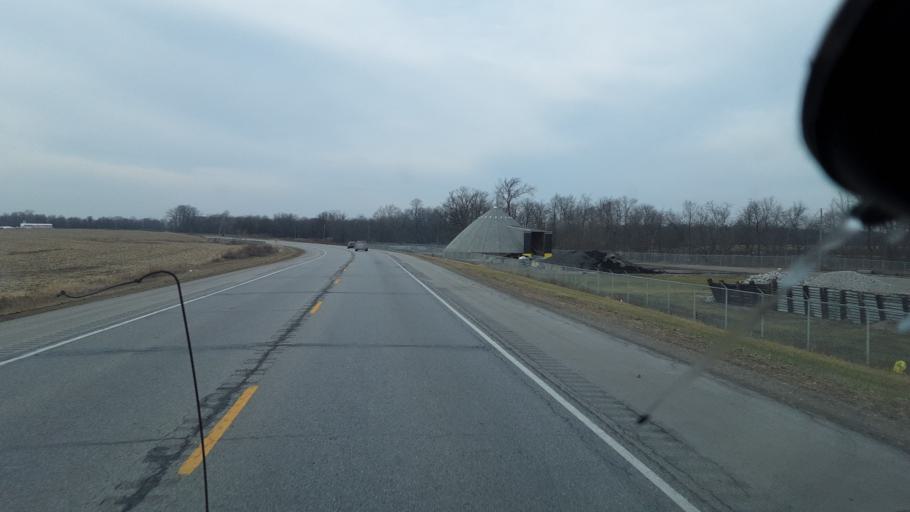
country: US
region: Indiana
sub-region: DeKalb County
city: Waterloo
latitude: 41.4376
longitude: -85.0357
